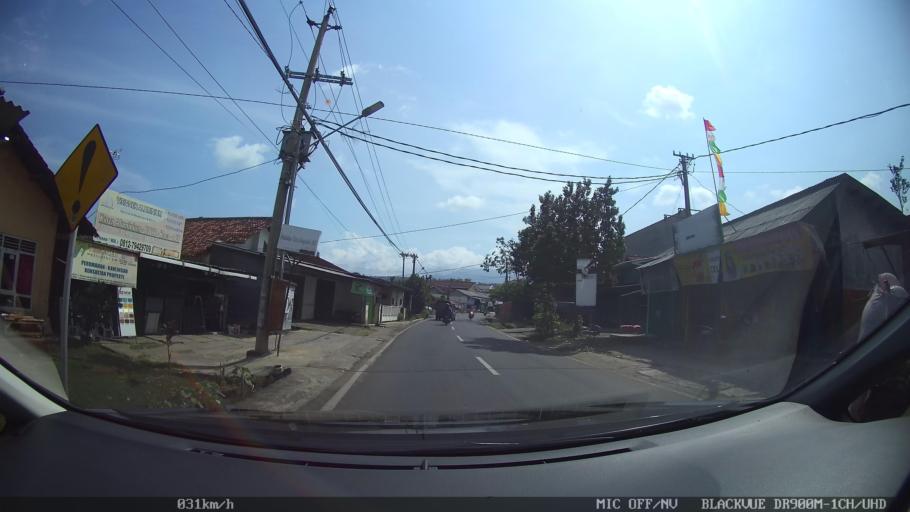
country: ID
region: Lampung
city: Kedaton
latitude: -5.3911
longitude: 105.2381
